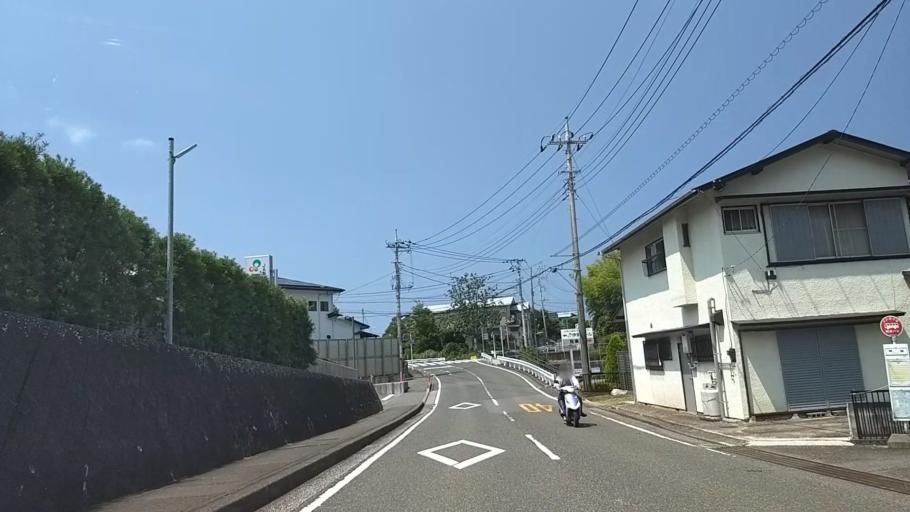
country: JP
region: Shizuoka
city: Ito
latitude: 34.9436
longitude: 139.1135
